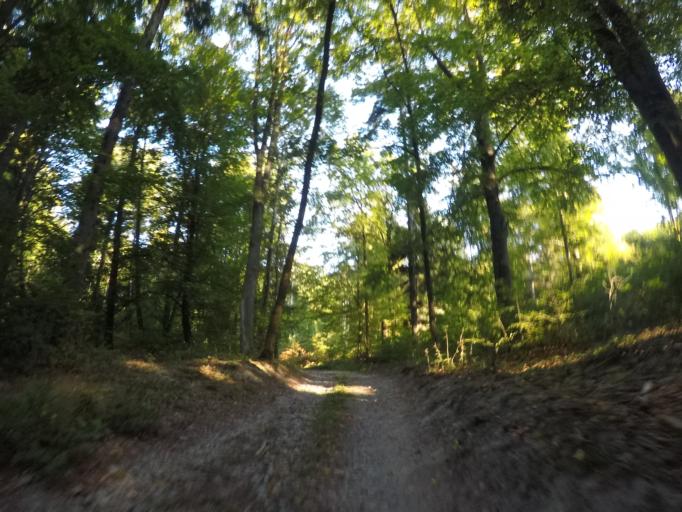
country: SK
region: Kosicky
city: Kosice
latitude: 48.7591
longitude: 21.1545
